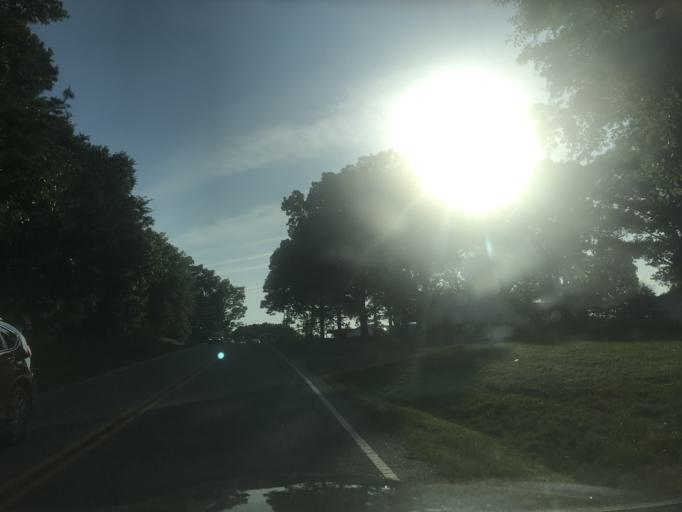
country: US
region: North Carolina
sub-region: Wake County
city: Knightdale
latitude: 35.7548
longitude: -78.5145
